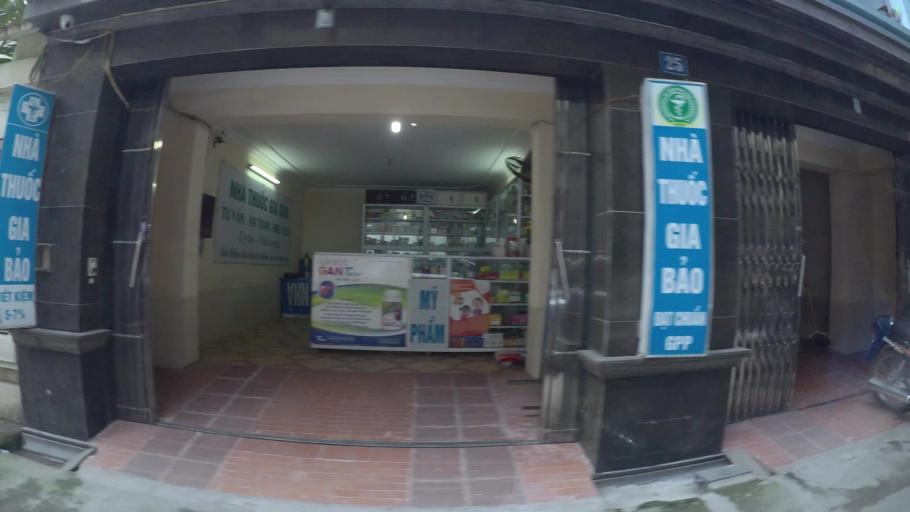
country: VN
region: Ha Noi
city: Tay Ho
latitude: 21.0529
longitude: 105.8054
